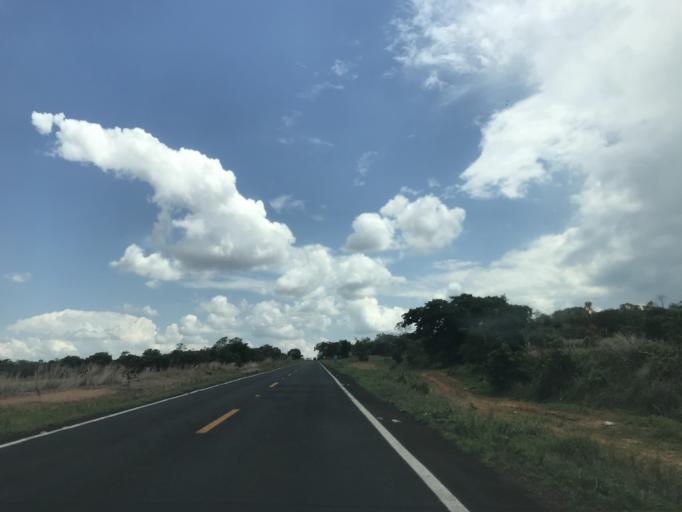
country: BR
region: Goias
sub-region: Caldas Novas
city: Caldas Novas
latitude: -17.6204
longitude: -48.7087
